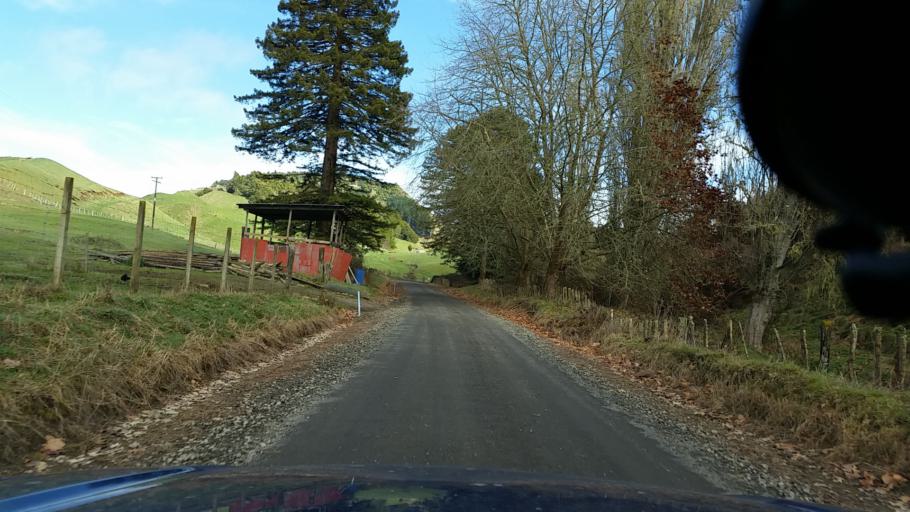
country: NZ
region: Taranaki
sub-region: New Plymouth District
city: Waitara
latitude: -39.0327
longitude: 174.7994
